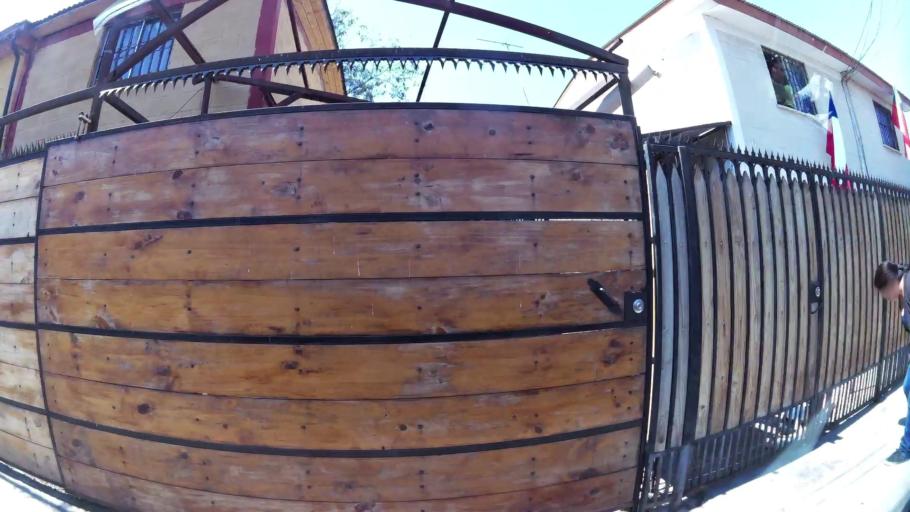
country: CL
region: Santiago Metropolitan
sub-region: Provincia de Santiago
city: Lo Prado
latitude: -33.3645
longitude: -70.7461
